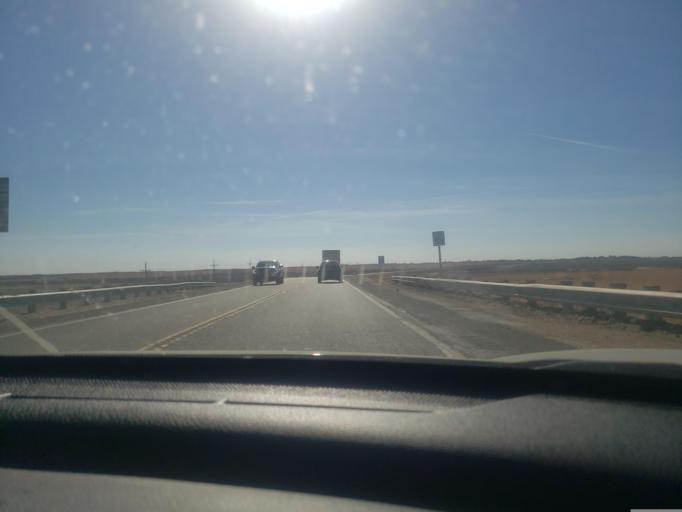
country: US
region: Kansas
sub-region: Finney County
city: Garden City
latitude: 37.9579
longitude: -100.8401
